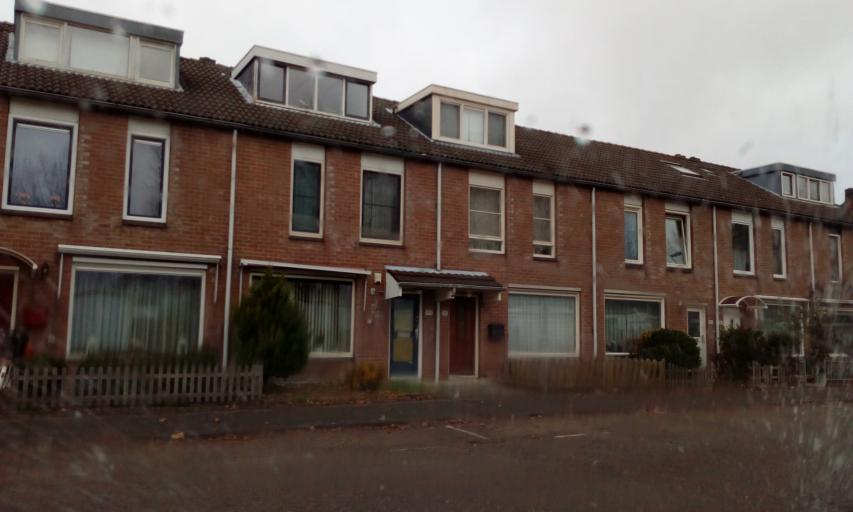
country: NL
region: South Holland
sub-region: Gemeente Capelle aan den IJssel
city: Capelle aan den IJssel
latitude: 51.9656
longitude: 4.5806
